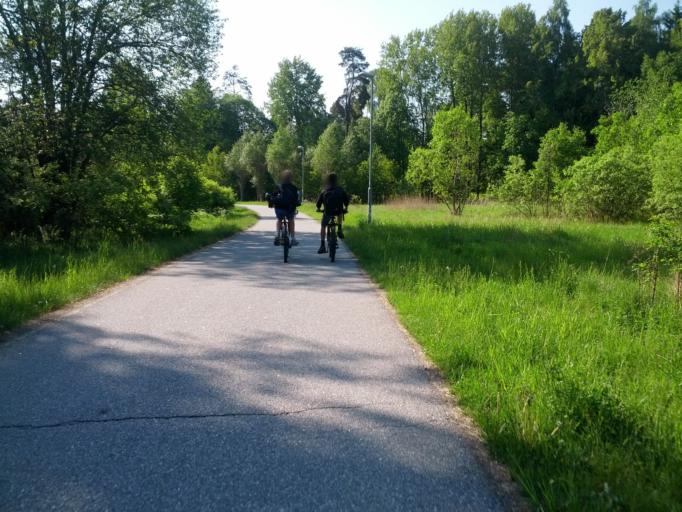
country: SE
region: Stockholm
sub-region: Danderyds Kommun
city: Djursholm
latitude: 59.4160
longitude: 18.0523
